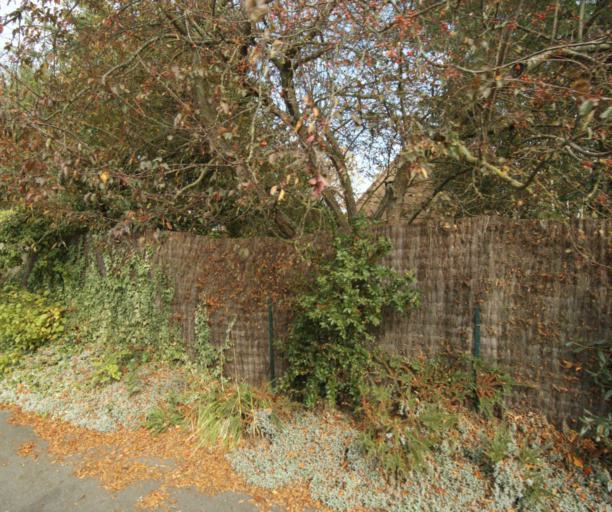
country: FR
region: Nord-Pas-de-Calais
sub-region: Departement du Pas-de-Calais
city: Billy-Berclau
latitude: 50.5332
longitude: 2.8638
